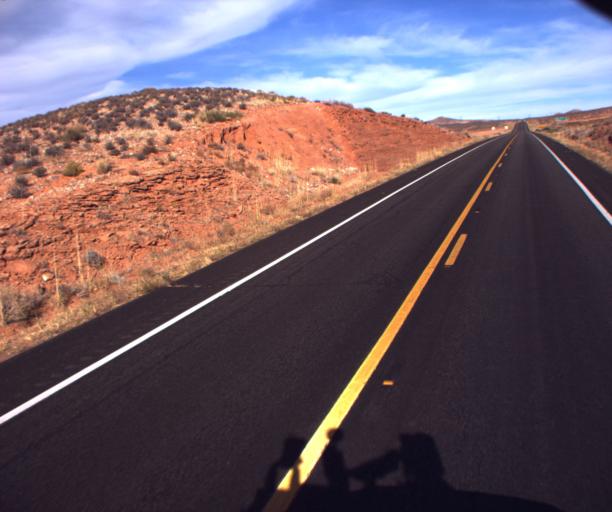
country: US
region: Arizona
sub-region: Apache County
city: Many Farms
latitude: 36.9315
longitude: -109.5715
